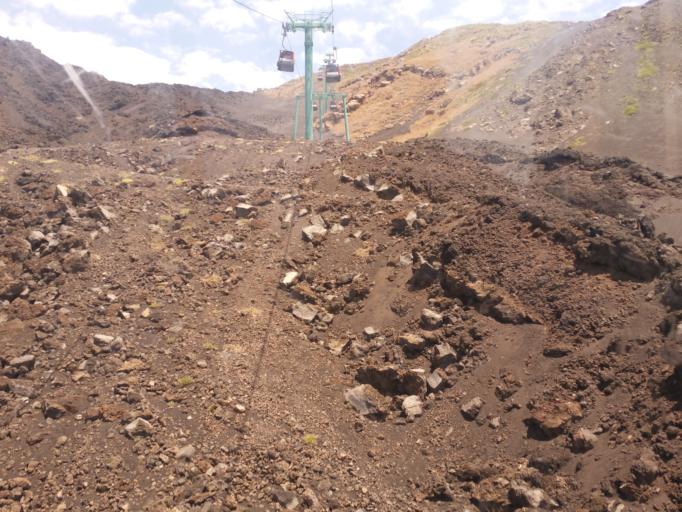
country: IT
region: Sicily
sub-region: Catania
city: Ragalna
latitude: 37.7098
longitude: 14.9995
